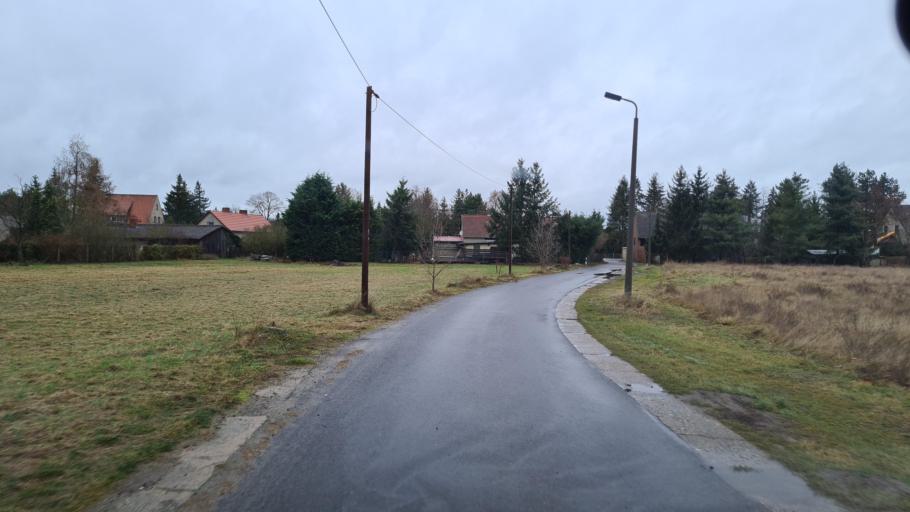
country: DE
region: Brandenburg
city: Luebben
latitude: 51.9457
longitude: 13.9183
